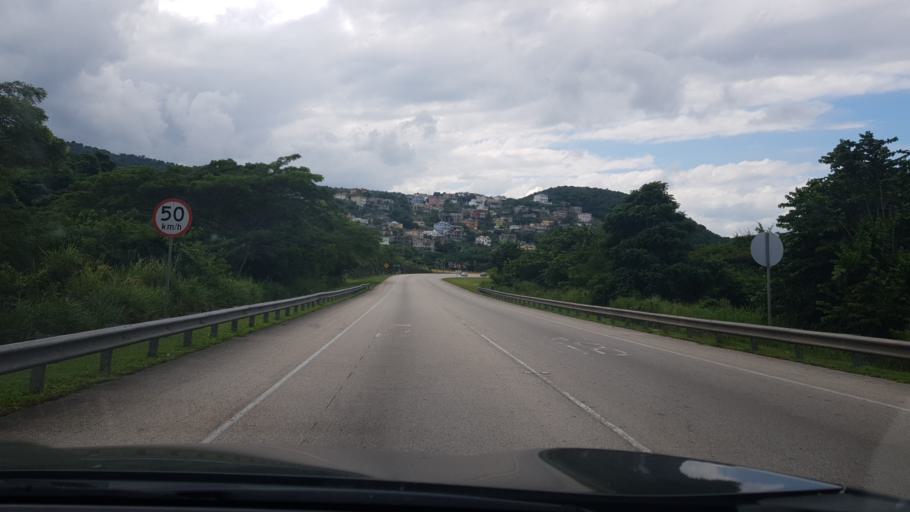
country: JM
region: Trelawny
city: Duncans
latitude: 18.4743
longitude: -77.5442
